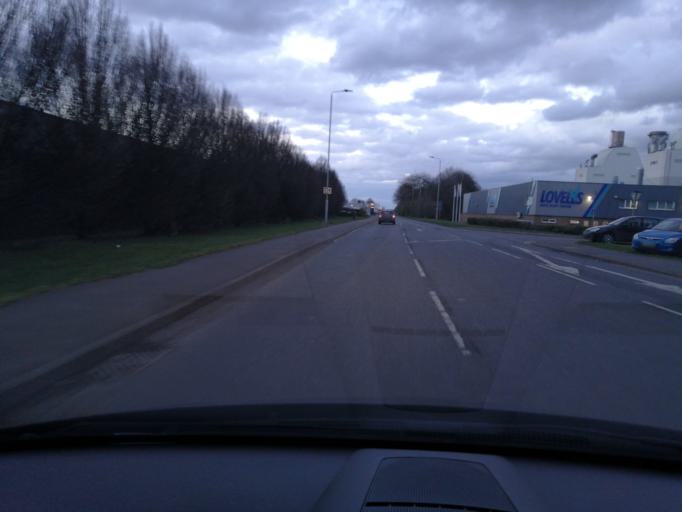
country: GB
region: England
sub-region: Peterborough
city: Eye
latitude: 52.5758
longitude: -0.2078
